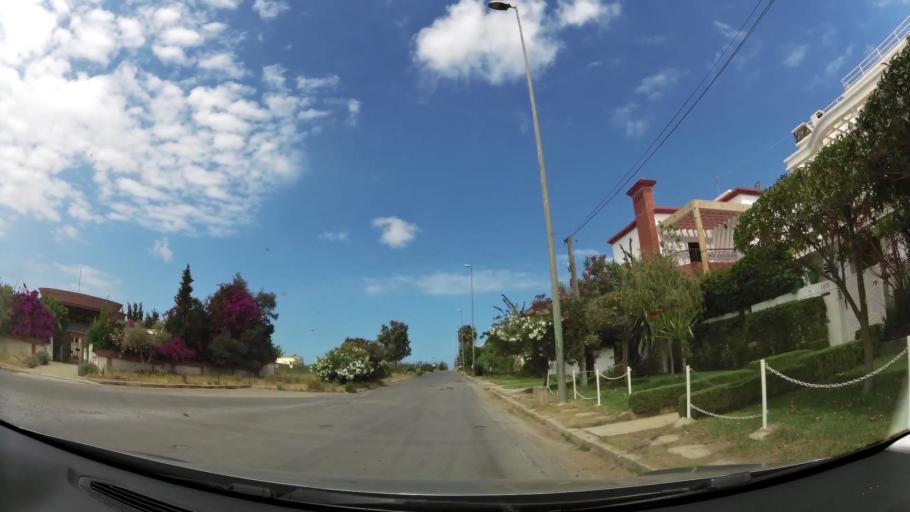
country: MA
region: Gharb-Chrarda-Beni Hssen
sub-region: Kenitra Province
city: Kenitra
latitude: 34.2414
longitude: -6.6035
